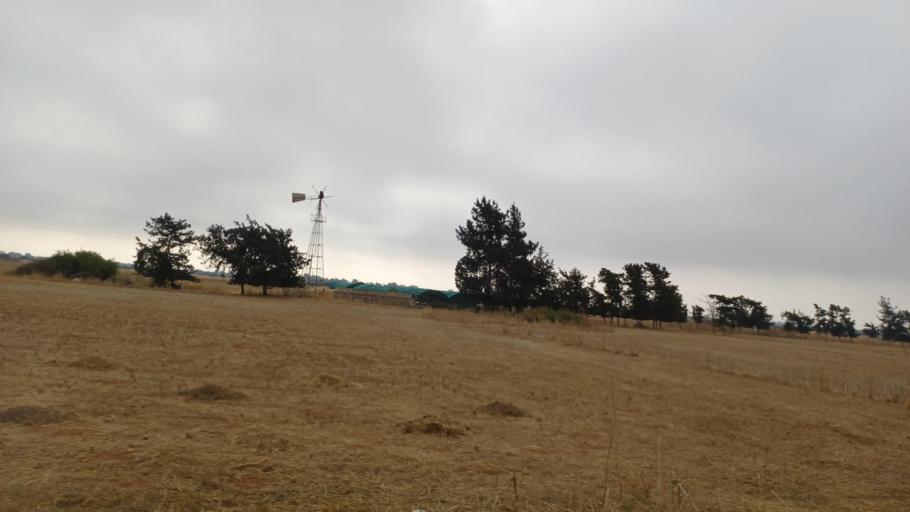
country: CY
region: Ammochostos
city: Achna
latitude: 35.0420
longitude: 33.7902
